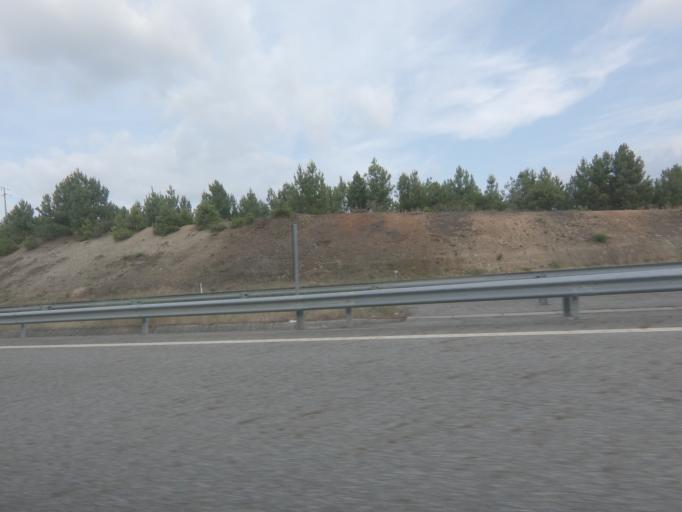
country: PT
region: Vila Real
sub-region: Chaves
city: Chaves
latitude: 41.6917
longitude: -7.5581
